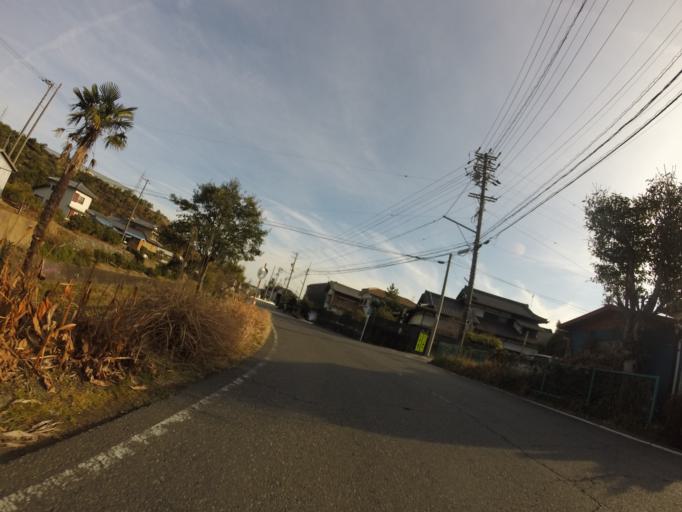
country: JP
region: Shizuoka
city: Shizuoka-shi
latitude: 35.0608
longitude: 138.4718
